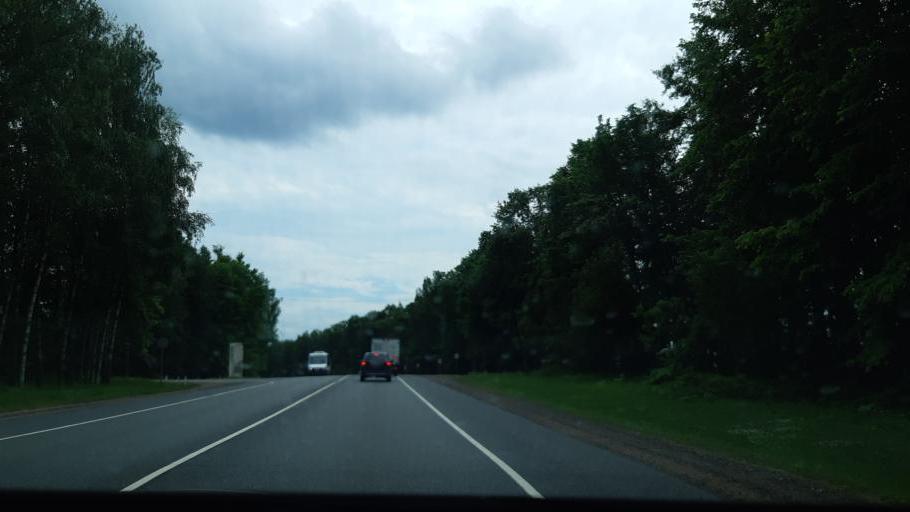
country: RU
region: Moskovskaya
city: Dorokhovo
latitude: 55.4973
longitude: 36.3483
